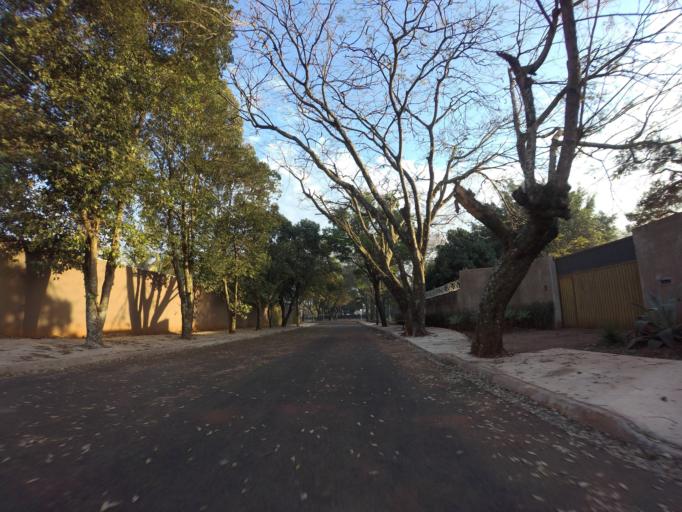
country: BR
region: Sao Paulo
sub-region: Piracicaba
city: Piracicaba
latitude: -22.7536
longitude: -47.5915
